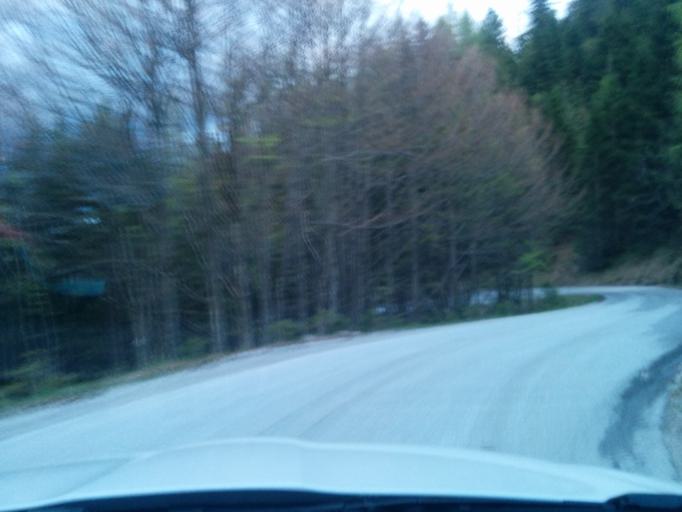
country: AT
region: Styria
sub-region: Politischer Bezirk Liezen
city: Aich
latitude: 47.4466
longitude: 13.8331
